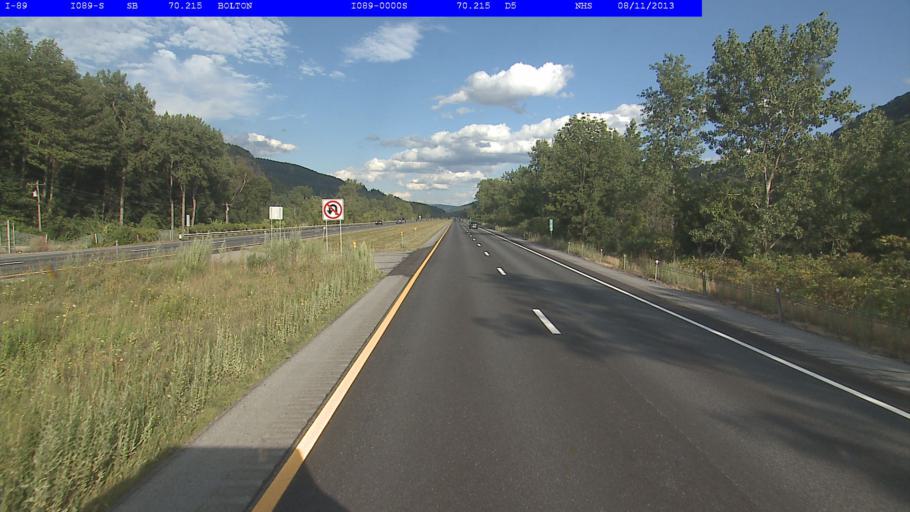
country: US
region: Vermont
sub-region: Washington County
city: Waterbury
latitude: 44.3709
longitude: -72.8725
